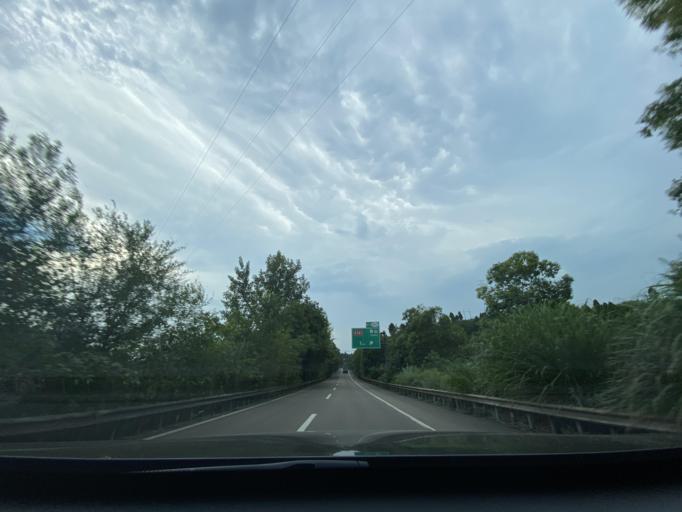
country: CN
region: Sichuan
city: Neijiang
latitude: 29.6797
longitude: 104.9604
